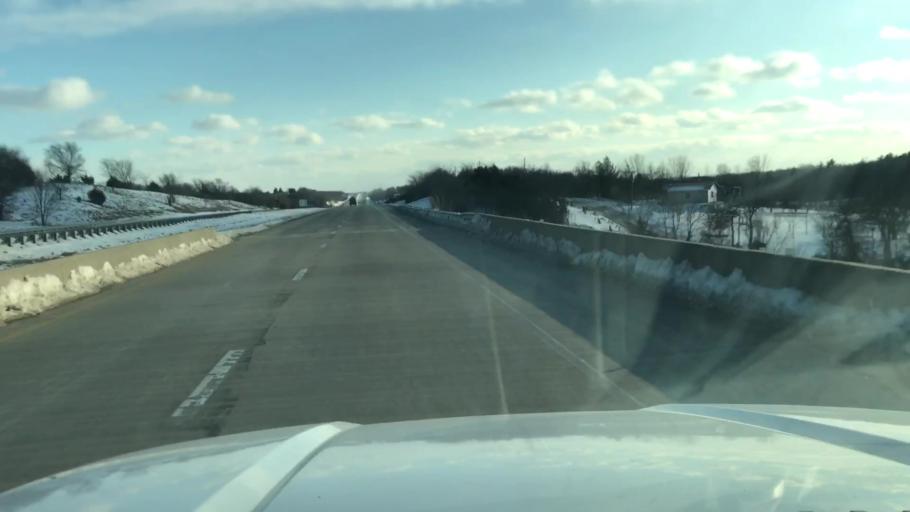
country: US
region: Missouri
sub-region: Andrew County
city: Savannah
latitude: 39.9483
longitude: -94.8603
